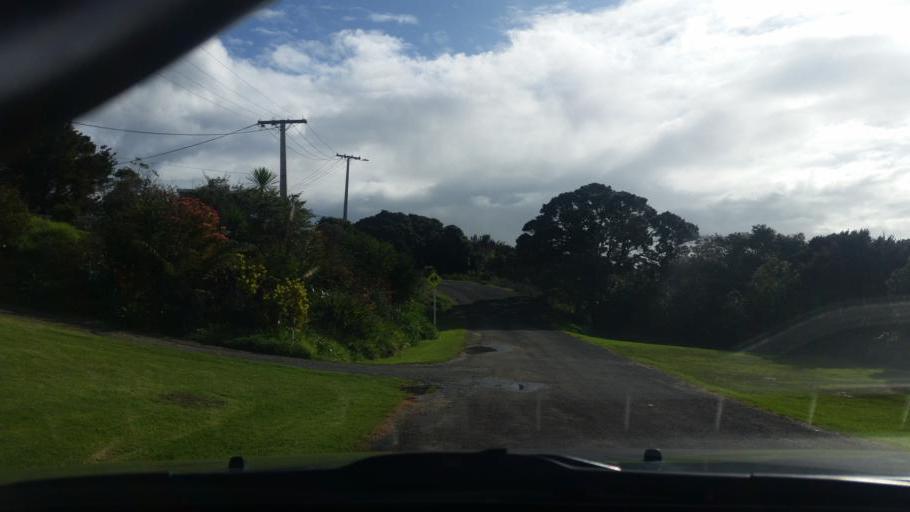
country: NZ
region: Auckland
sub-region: Auckland
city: Wellsford
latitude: -36.2567
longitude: 174.2508
